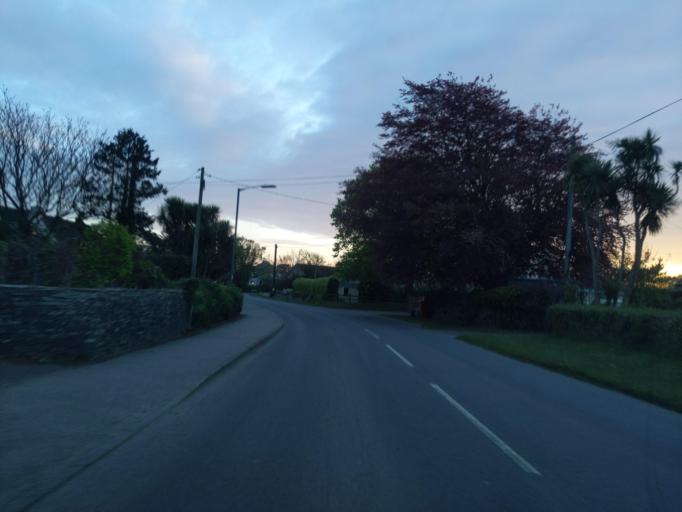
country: GB
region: England
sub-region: Cornwall
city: Polzeath
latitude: 50.5514
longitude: -4.9003
